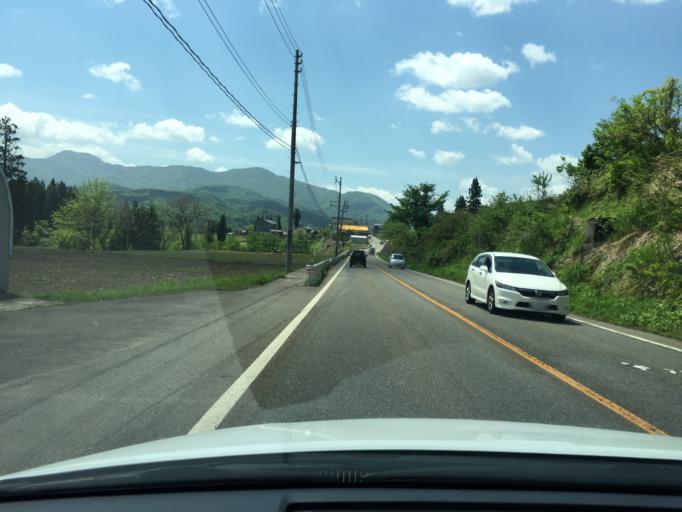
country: JP
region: Niigata
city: Tochio-honcho
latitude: 37.3328
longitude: 139.0277
